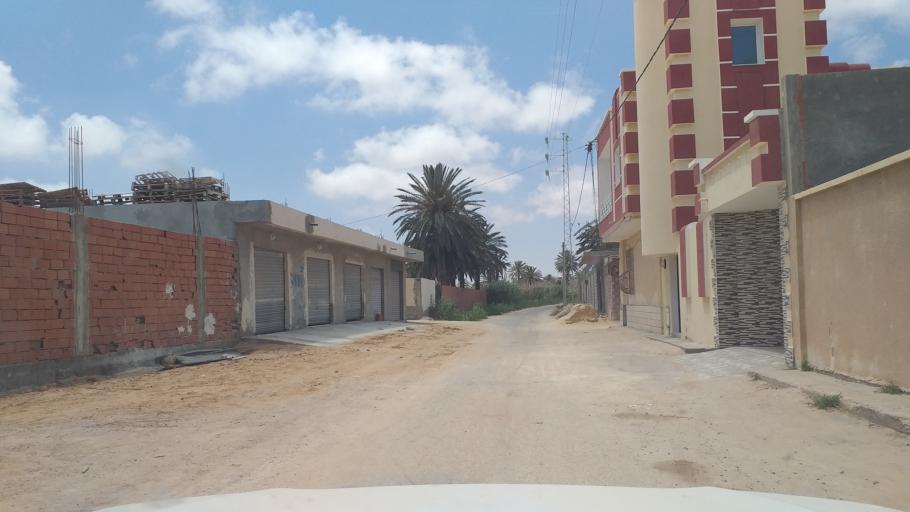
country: TN
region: Qabis
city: Gabes
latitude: 33.9325
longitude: 10.0578
